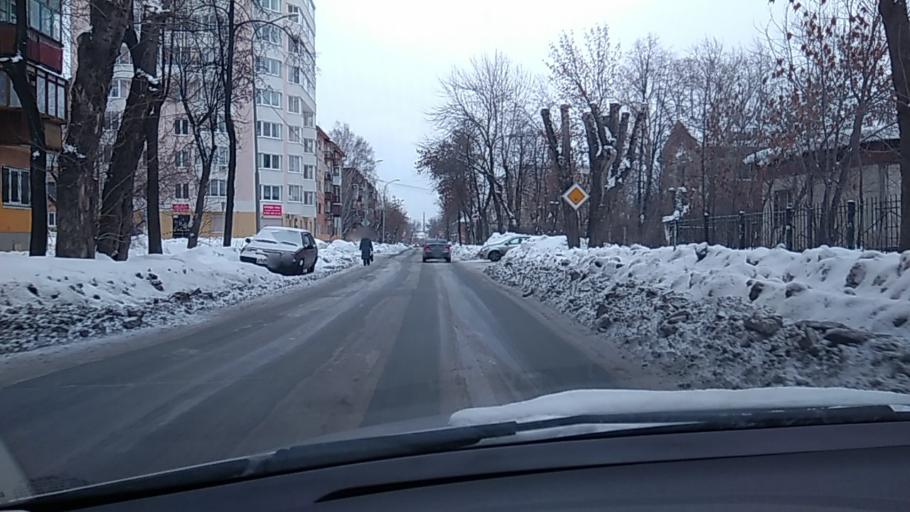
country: RU
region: Sverdlovsk
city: Yekaterinburg
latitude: 56.8886
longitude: 60.5749
